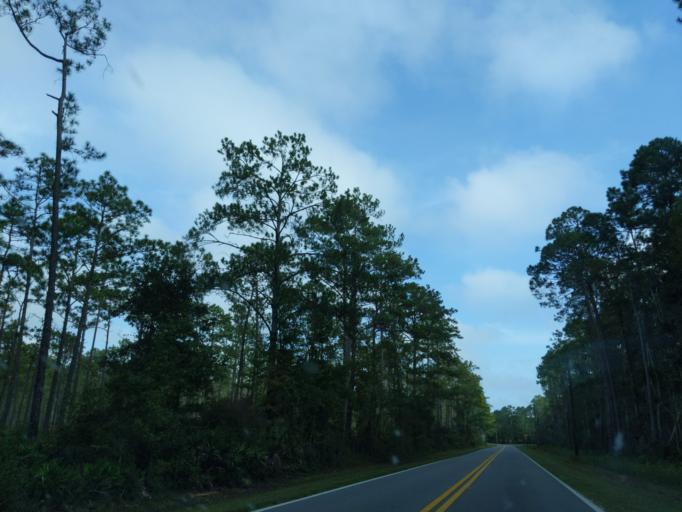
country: US
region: Florida
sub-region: Wakulla County
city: Crawfordville
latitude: 30.1042
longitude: -84.3070
